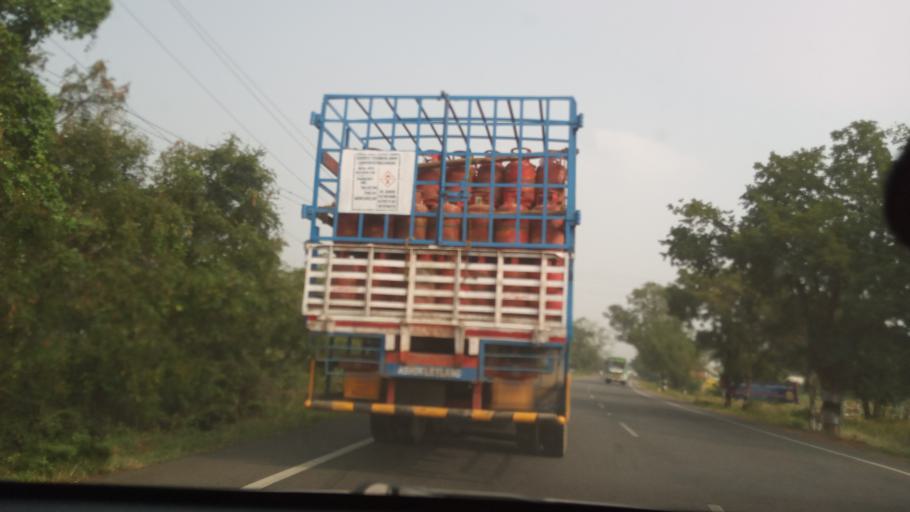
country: IN
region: Tamil Nadu
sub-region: Erode
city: Punjai Puliyampatti
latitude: 11.3728
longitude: 77.1712
